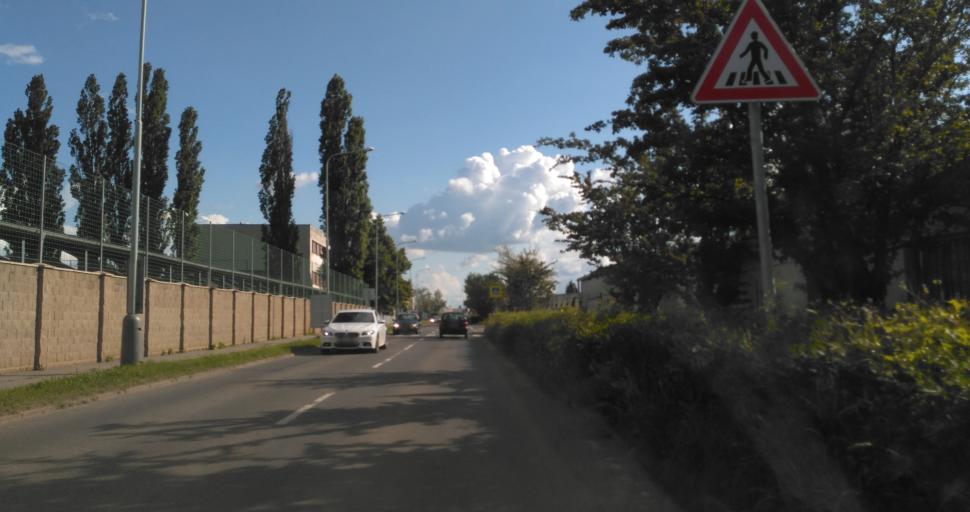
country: CZ
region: Praha
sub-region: Praha 19
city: Satalice
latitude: 50.1231
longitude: 14.5665
